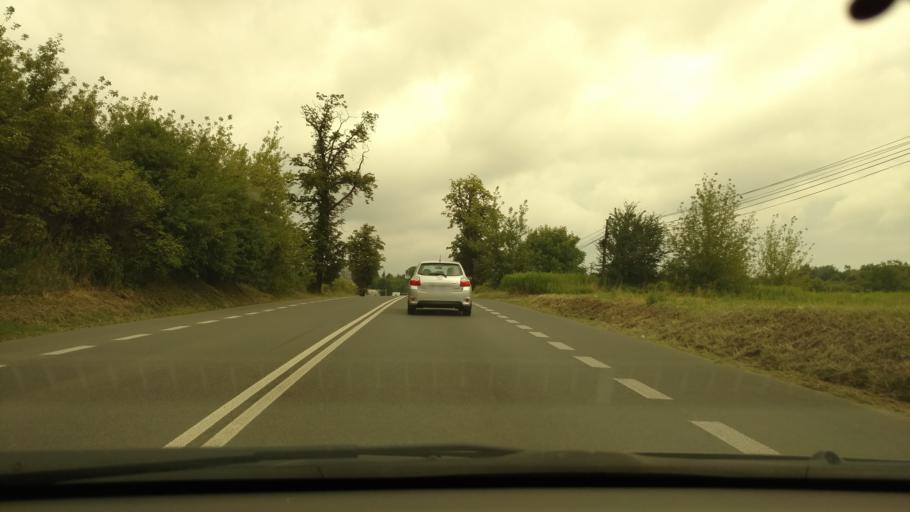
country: PL
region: Lesser Poland Voivodeship
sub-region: Powiat krakowski
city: Zielonki
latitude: 50.1034
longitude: 19.9640
